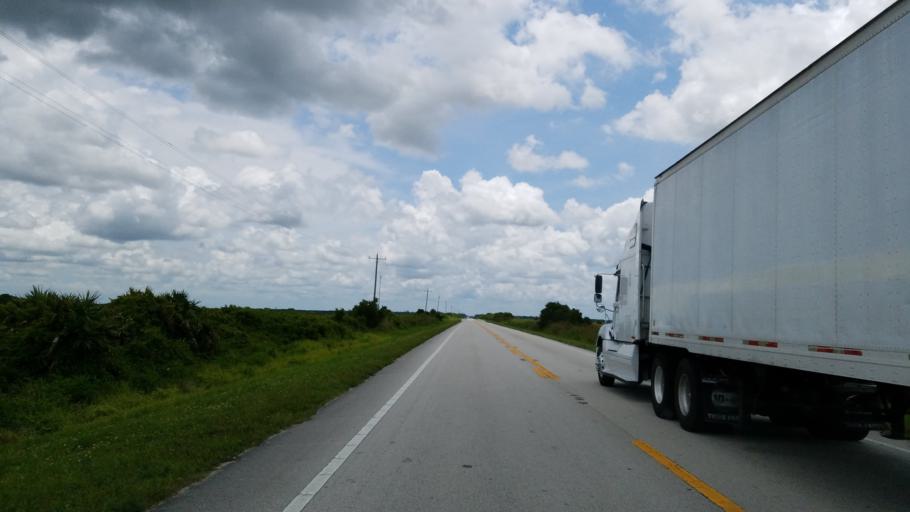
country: US
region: Florida
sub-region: Polk County
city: Babson Park
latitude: 27.7883
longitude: -81.1479
